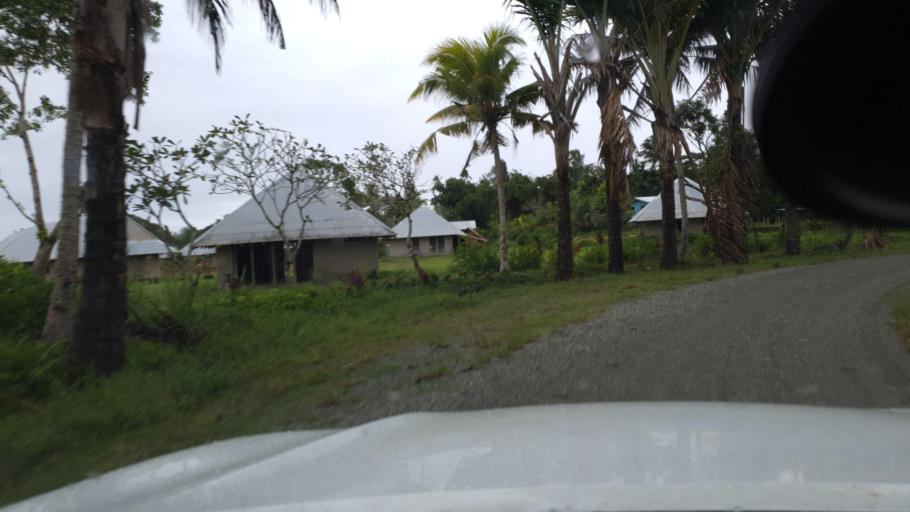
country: SB
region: Central Province
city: Tulaghi
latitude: -9.4485
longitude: 160.3921
